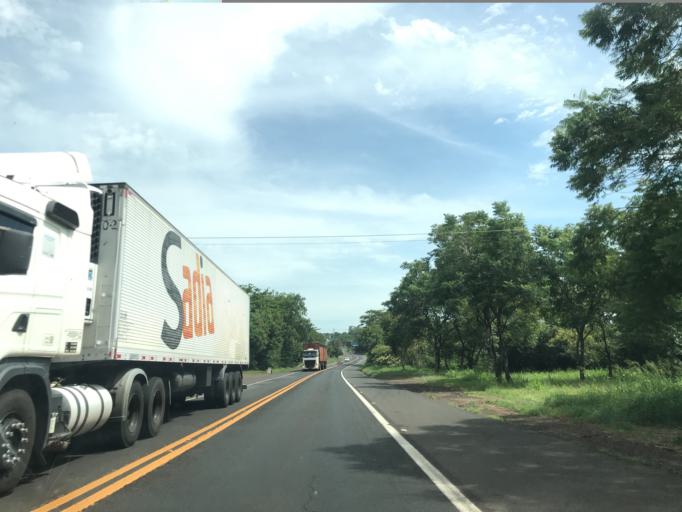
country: BR
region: Sao Paulo
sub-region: Nova Granada
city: Nova Granada
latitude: -20.3112
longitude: -49.2088
